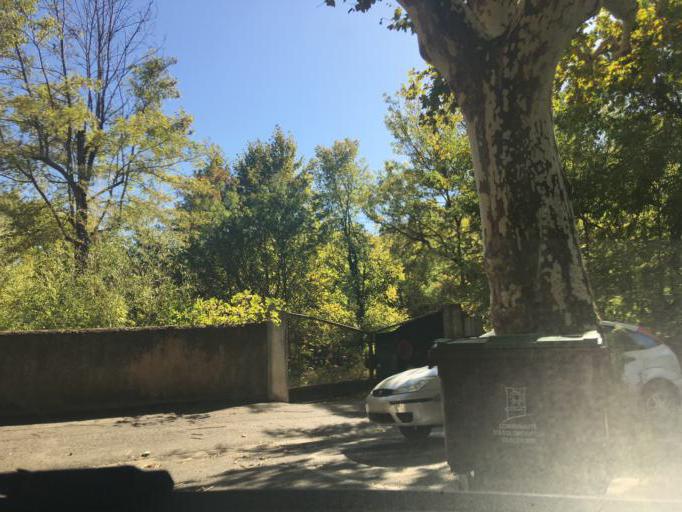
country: FR
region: Provence-Alpes-Cote d'Azur
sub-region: Departement du Var
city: Salernes
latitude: 43.5642
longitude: 6.2296
